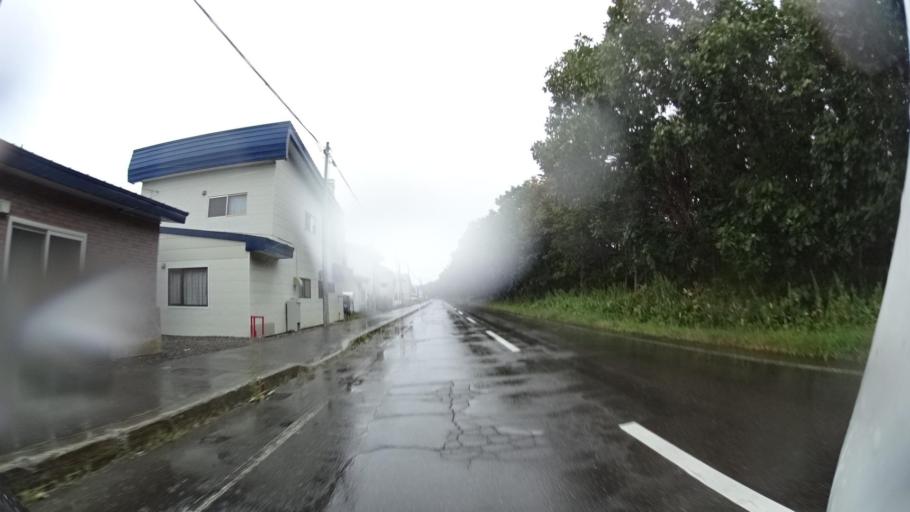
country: JP
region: Hokkaido
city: Mombetsu
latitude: 44.3315
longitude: 143.4913
